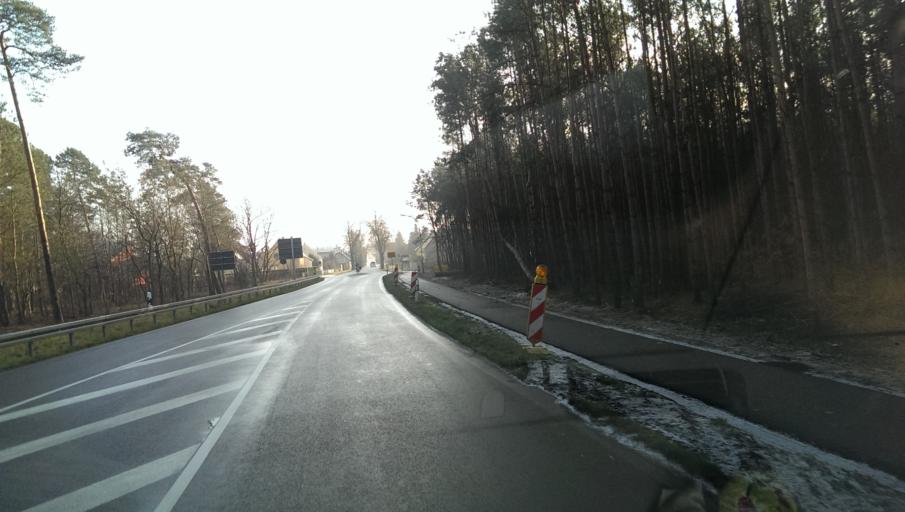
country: DE
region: Brandenburg
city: Bad Liebenwerda
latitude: 51.5516
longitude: 13.3797
